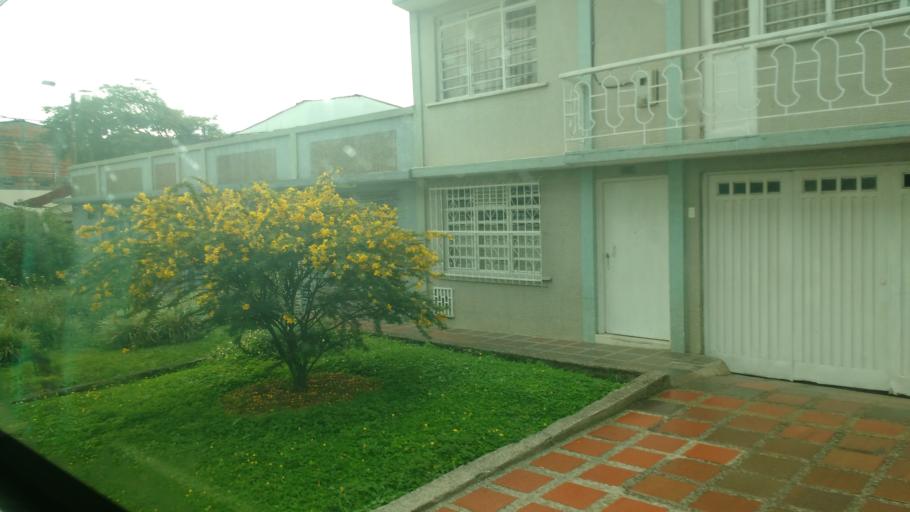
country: CO
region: Risaralda
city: Pereira
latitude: 4.8126
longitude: -75.7060
